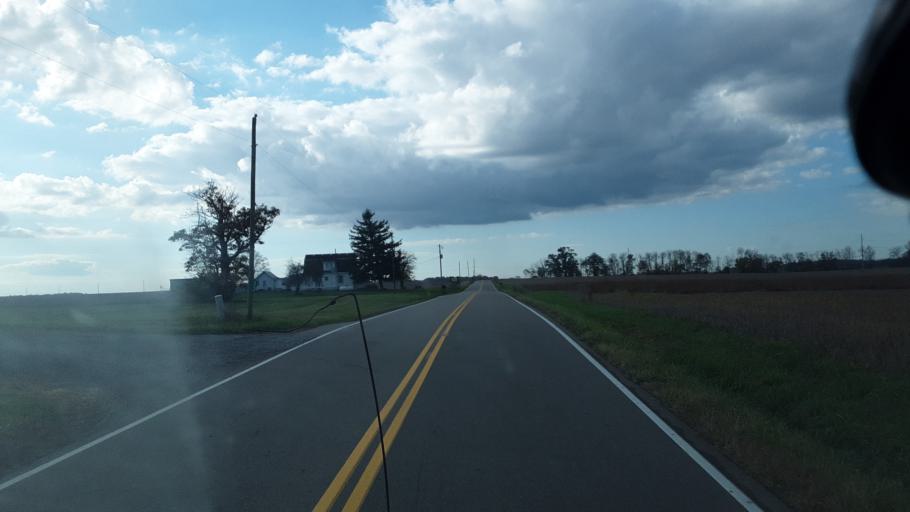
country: US
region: Ohio
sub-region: Fayette County
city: Washington Court House
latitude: 39.4396
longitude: -83.4388
